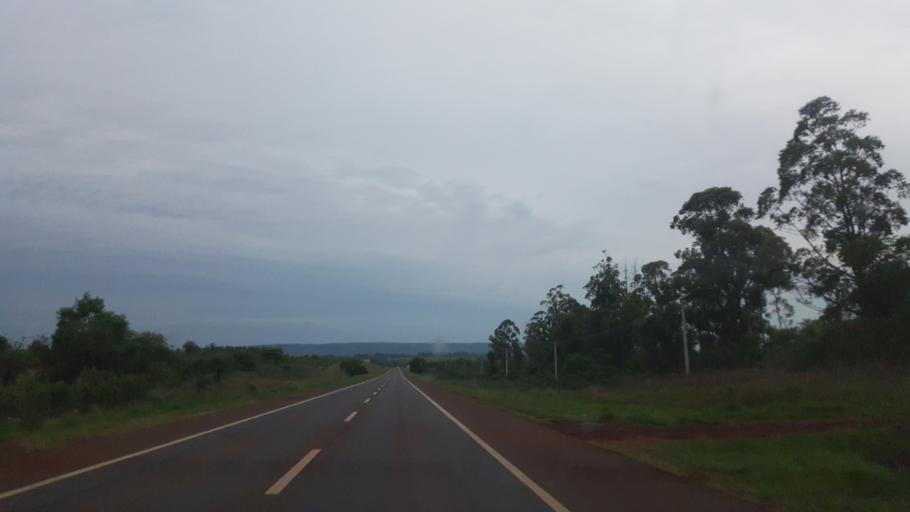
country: AR
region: Misiones
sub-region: Departamento de Apostoles
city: San Jose
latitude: -27.7750
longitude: -55.8085
